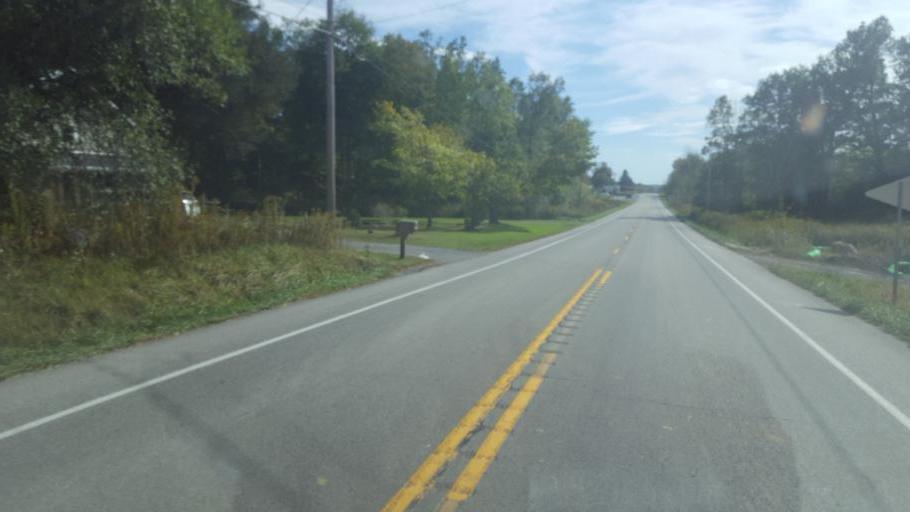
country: US
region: Pennsylvania
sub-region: Mercer County
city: Mercer
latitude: 41.3234
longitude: -80.2307
